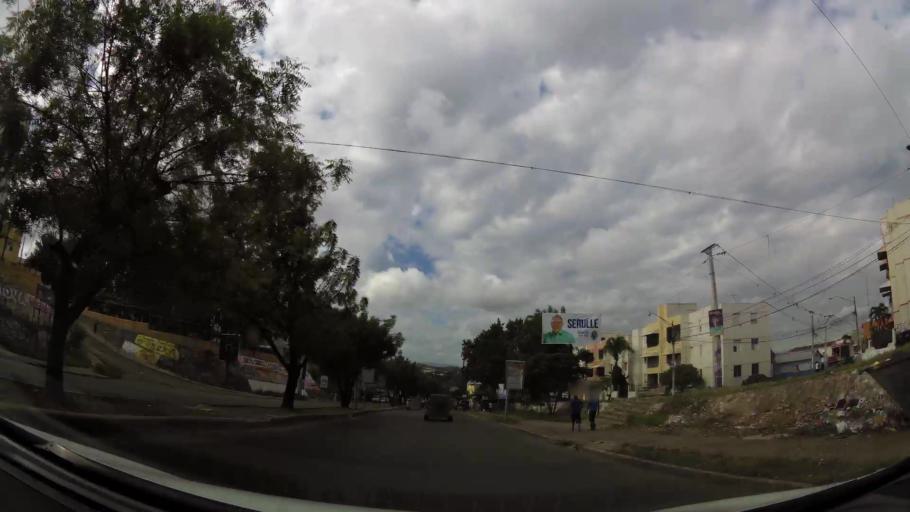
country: DO
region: Santiago
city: Santiago de los Caballeros
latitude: 19.4285
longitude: -70.6951
